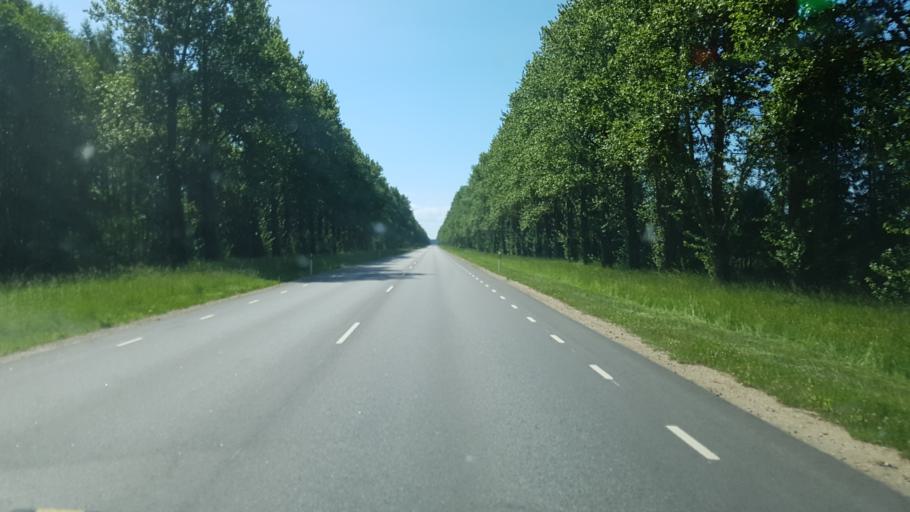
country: EE
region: Polvamaa
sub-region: Polva linn
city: Polva
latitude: 58.2975
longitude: 27.0014
